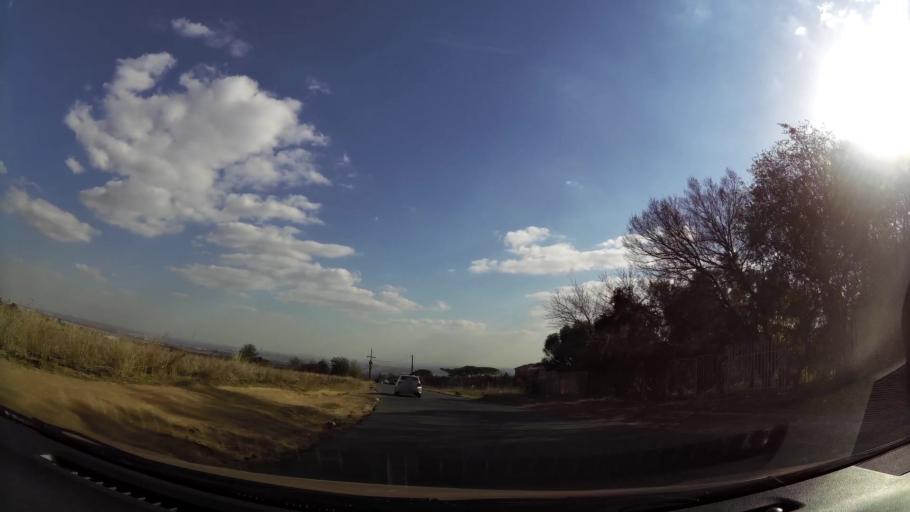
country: ZA
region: Gauteng
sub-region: City of Johannesburg Metropolitan Municipality
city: Midrand
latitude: -26.0134
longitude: 28.1608
